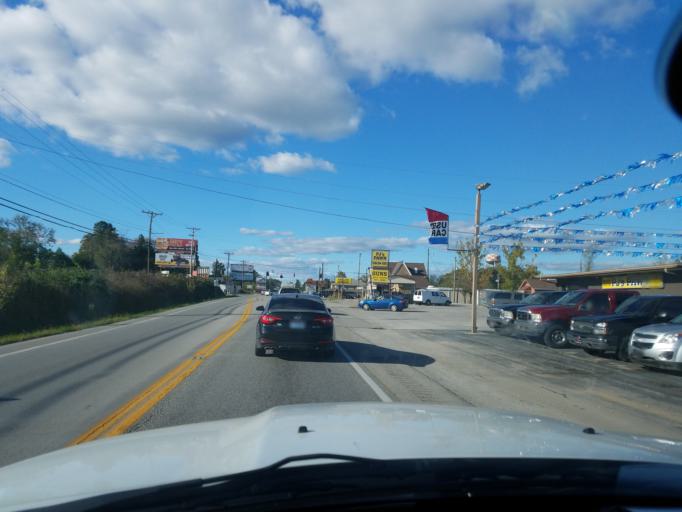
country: US
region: Kentucky
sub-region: Laurel County
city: London
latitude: 37.0867
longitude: -84.0620
